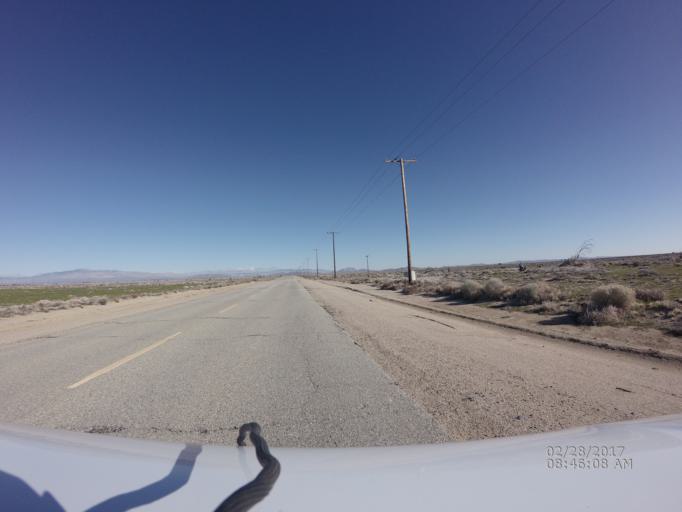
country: US
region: California
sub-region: Kern County
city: Rosamond
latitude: 34.7685
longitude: -118.2373
